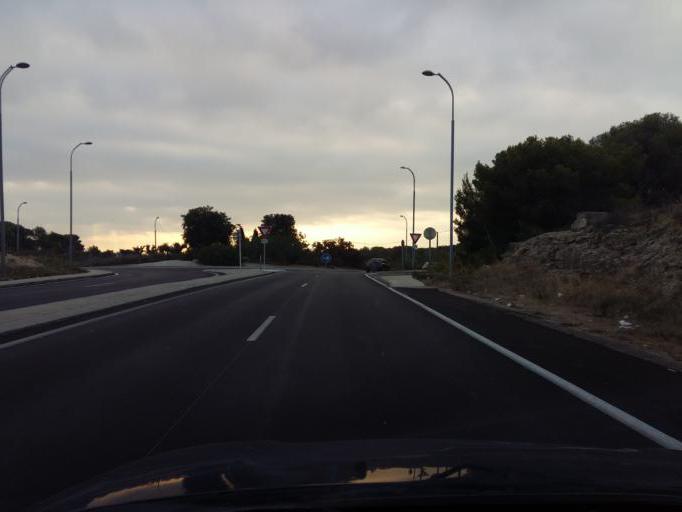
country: FR
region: Provence-Alpes-Cote d'Azur
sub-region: Departement des Bouches-du-Rhone
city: Saint-Mitre-les-Remparts
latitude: 43.4346
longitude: 5.0394
